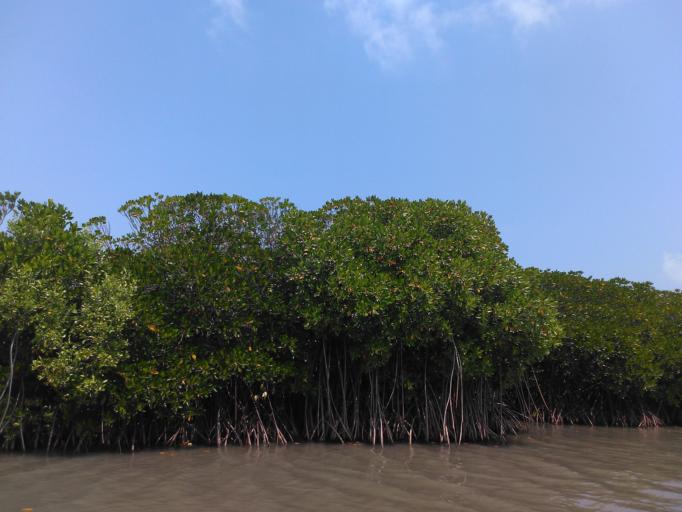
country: IN
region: Tamil Nadu
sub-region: Cuddalore
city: Annamalainagar
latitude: 11.4442
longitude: 79.7926
